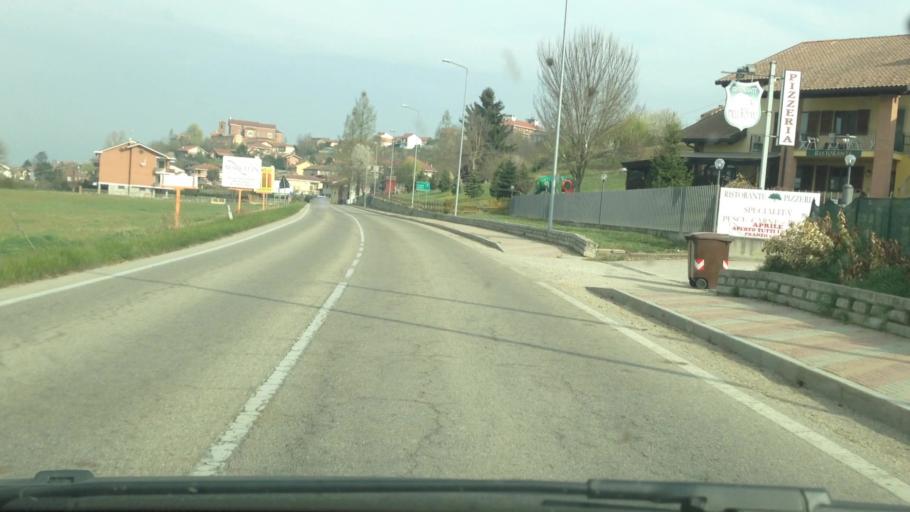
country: IT
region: Piedmont
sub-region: Provincia di Torino
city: Pralormo
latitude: 44.8549
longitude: 7.9071
